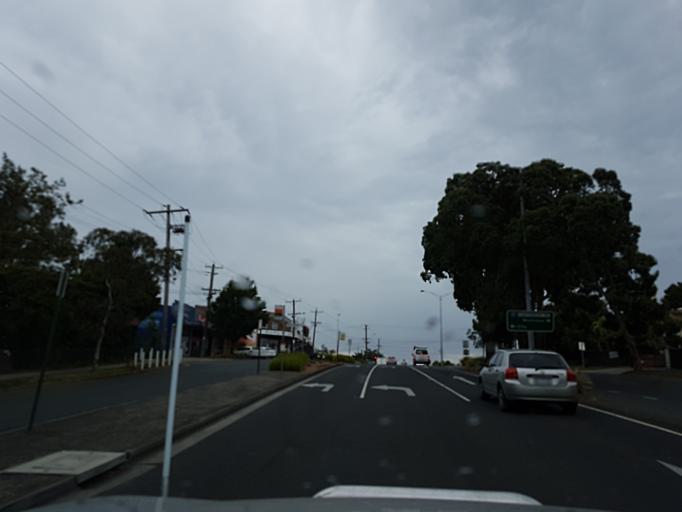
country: AU
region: Victoria
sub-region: Whitehorse
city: Vermont
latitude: -37.8371
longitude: 145.1965
